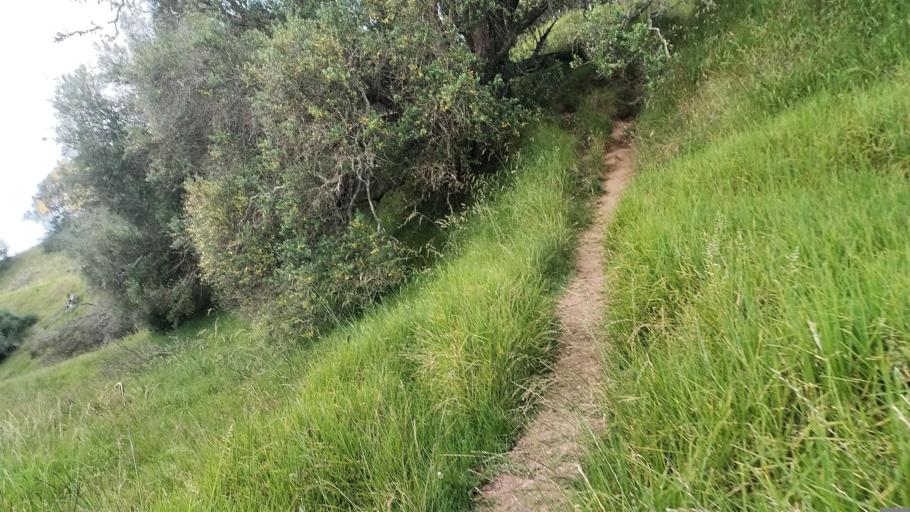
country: NZ
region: Auckland
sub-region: Auckland
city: Auckland
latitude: -36.8985
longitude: 174.7824
